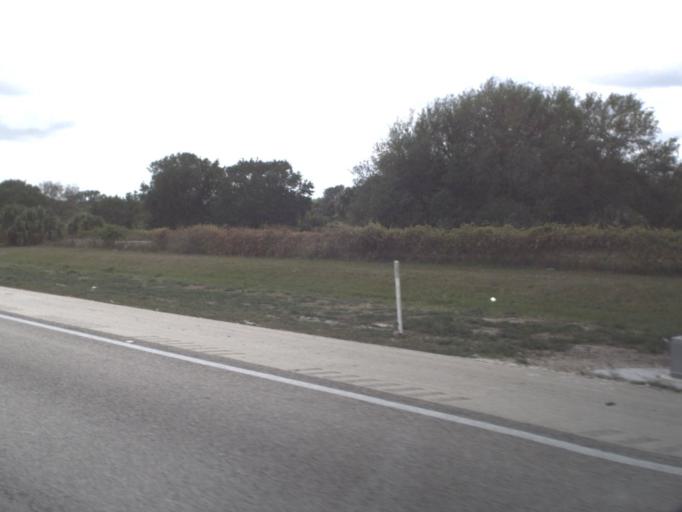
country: US
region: Florida
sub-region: Brevard County
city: South Patrick Shores
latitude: 28.2006
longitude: -80.7101
